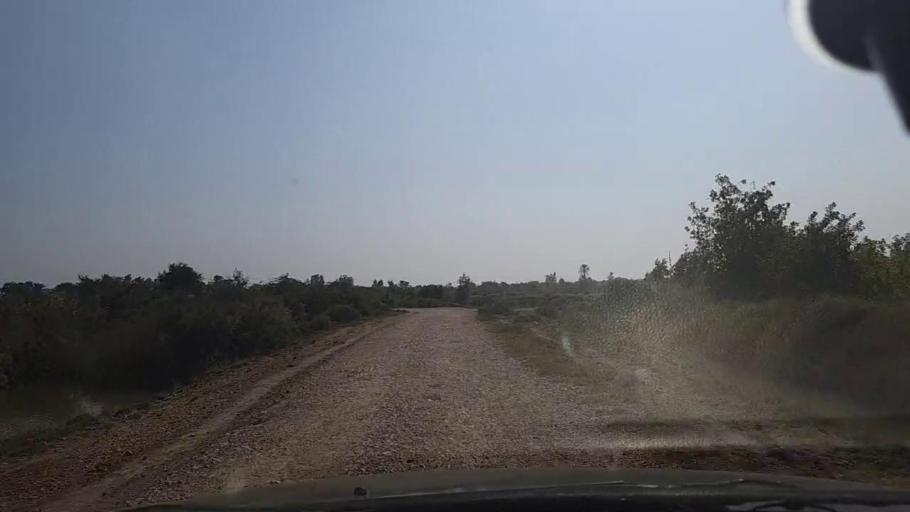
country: PK
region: Sindh
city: Chuhar Jamali
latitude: 24.5180
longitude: 67.8836
